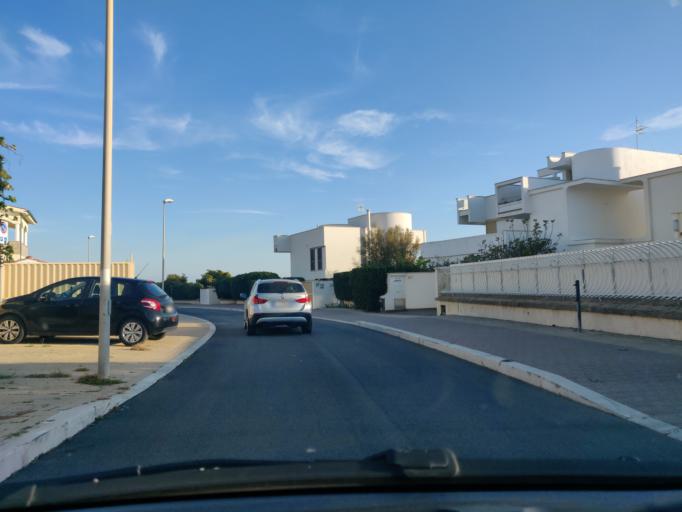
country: IT
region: Latium
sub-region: Citta metropolitana di Roma Capitale
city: Santa Marinella
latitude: 42.0301
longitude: 11.8354
